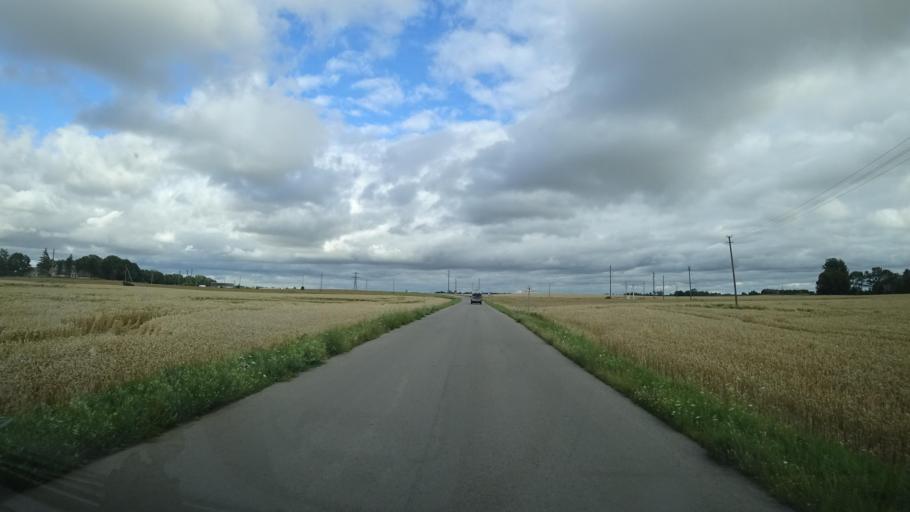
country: LT
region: Marijampoles apskritis
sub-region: Marijampole Municipality
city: Marijampole
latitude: 54.5182
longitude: 23.3244
